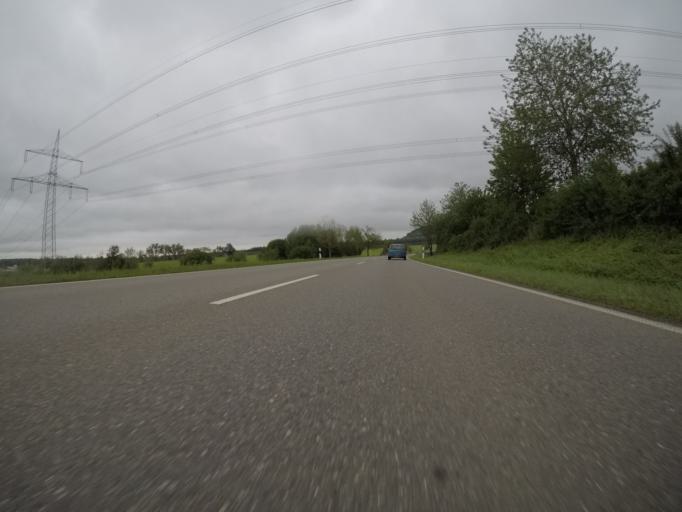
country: DE
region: Baden-Wuerttemberg
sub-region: Regierungsbezirk Stuttgart
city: Weilheim an der Teck
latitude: 48.6275
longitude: 9.5483
